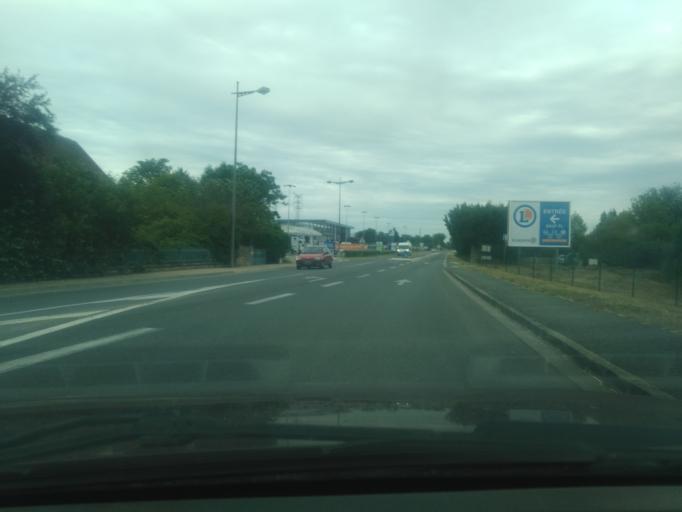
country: FR
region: Centre
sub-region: Departement du Cher
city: Saint-Amand-Montrond
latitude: 46.7217
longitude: 2.5306
